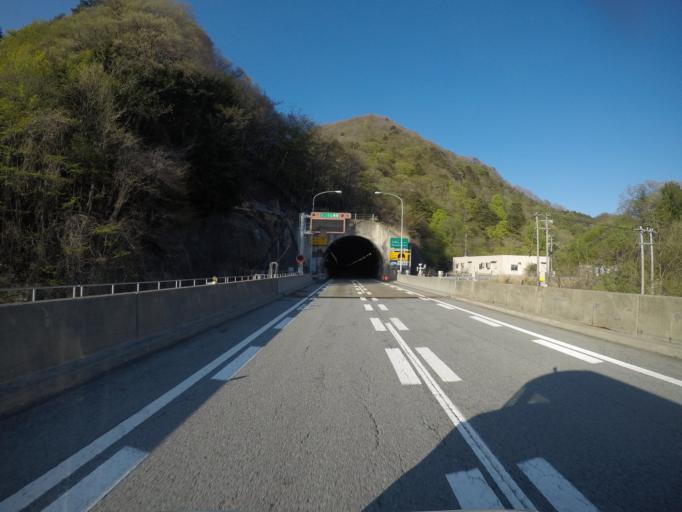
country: JP
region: Nagano
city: Saku
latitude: 36.2811
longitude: 138.6248
